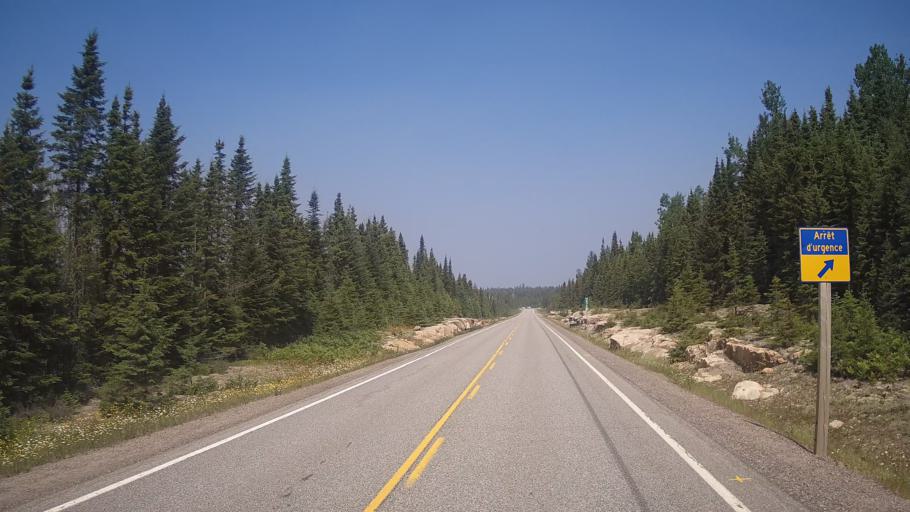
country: CA
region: Ontario
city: Timmins
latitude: 48.0685
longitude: -81.5896
